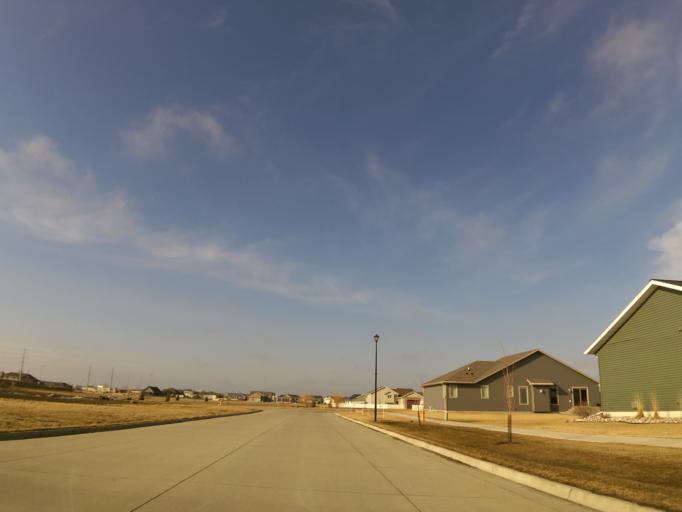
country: US
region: North Dakota
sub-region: Grand Forks County
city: Grand Forks
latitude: 47.8797
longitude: -97.0642
